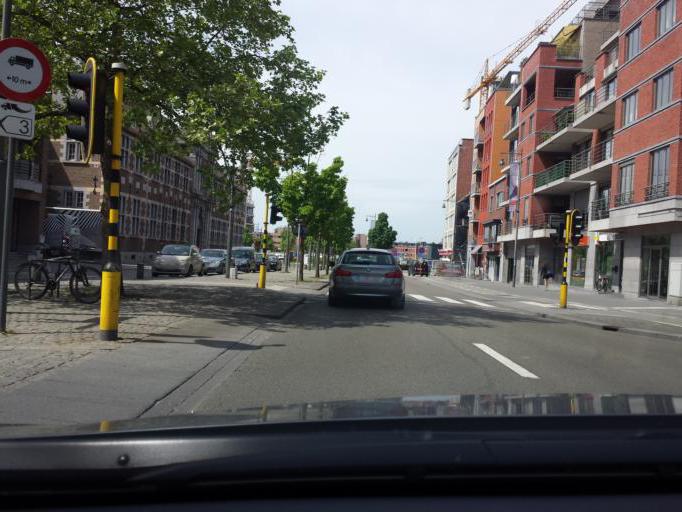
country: BE
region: Flanders
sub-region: Provincie Limburg
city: Hasselt
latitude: 50.9341
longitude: 5.3395
